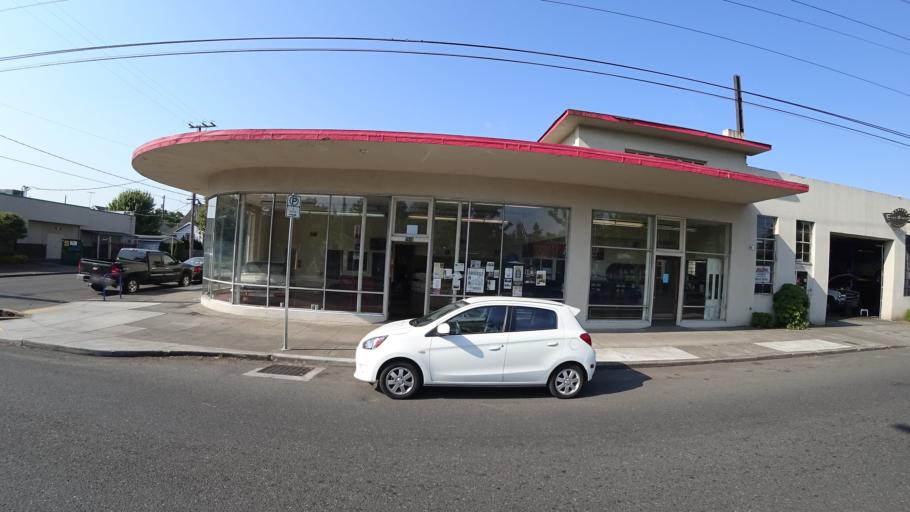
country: US
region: Oregon
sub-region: Washington County
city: West Haven
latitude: 45.5890
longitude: -122.7469
